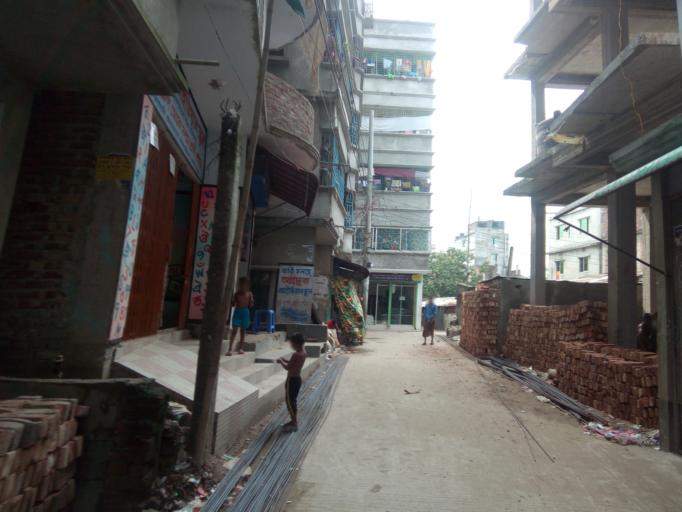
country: BD
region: Dhaka
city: Azimpur
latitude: 23.7176
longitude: 90.3674
